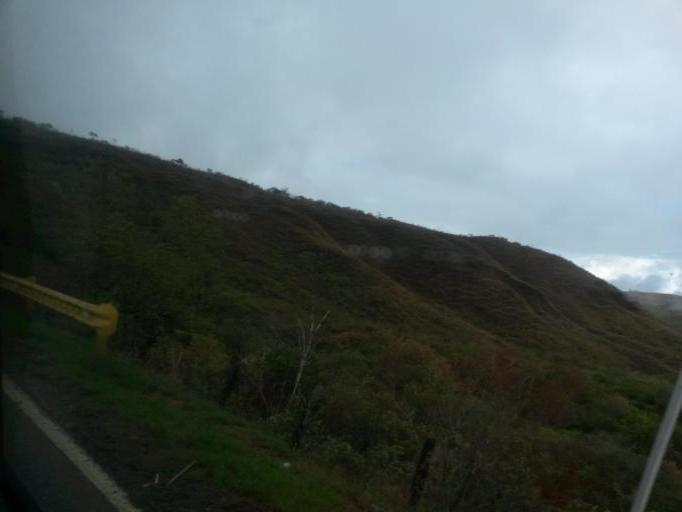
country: CO
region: Cauca
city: El Bordo
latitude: 2.1567
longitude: -76.9136
